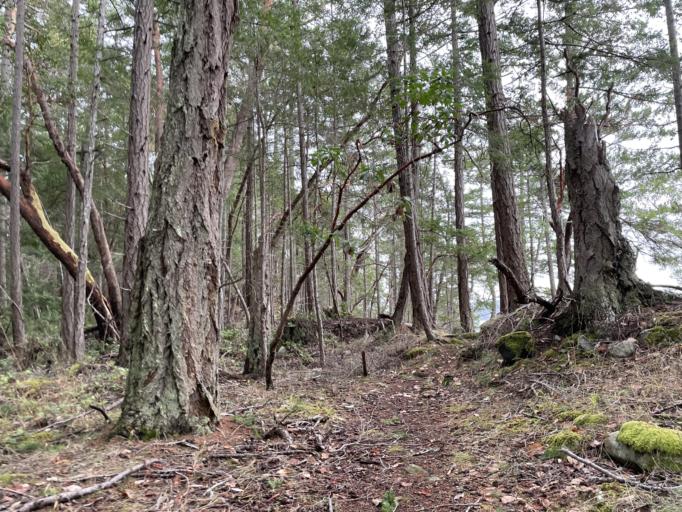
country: CA
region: British Columbia
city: North Cowichan
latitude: 48.9400
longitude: -123.5518
